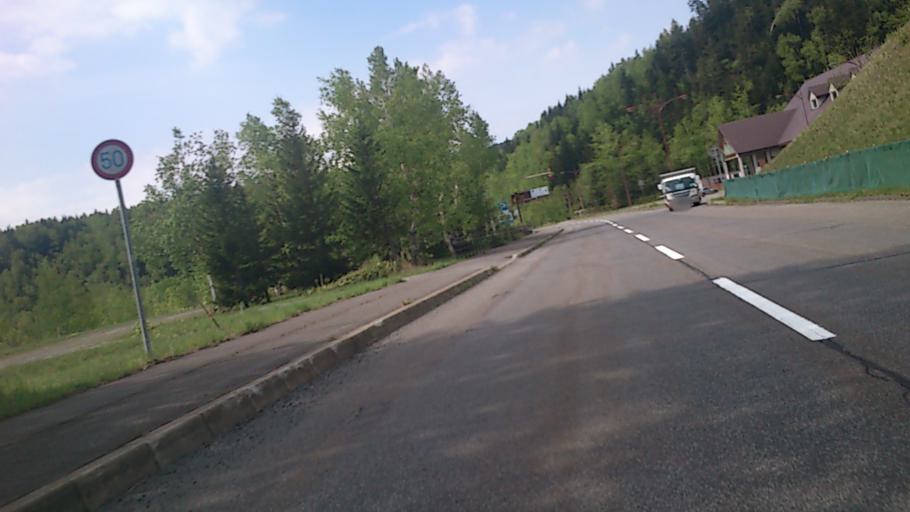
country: JP
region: Hokkaido
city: Kamikawa
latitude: 43.6664
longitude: 143.0372
